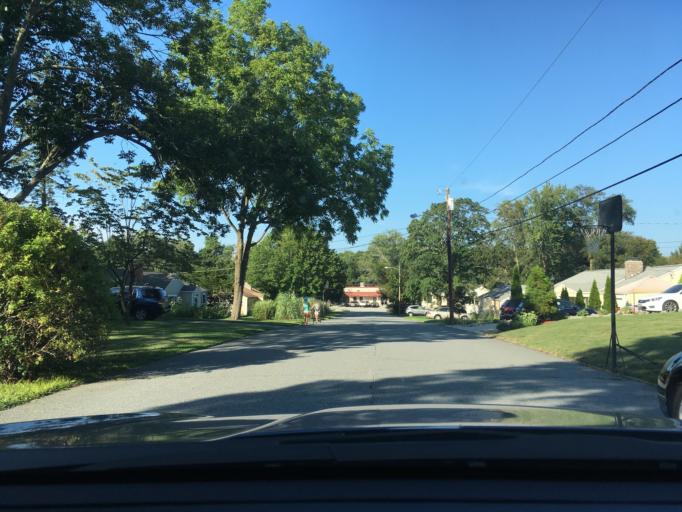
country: US
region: Rhode Island
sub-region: Kent County
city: East Greenwich
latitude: 41.6499
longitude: -71.4621
